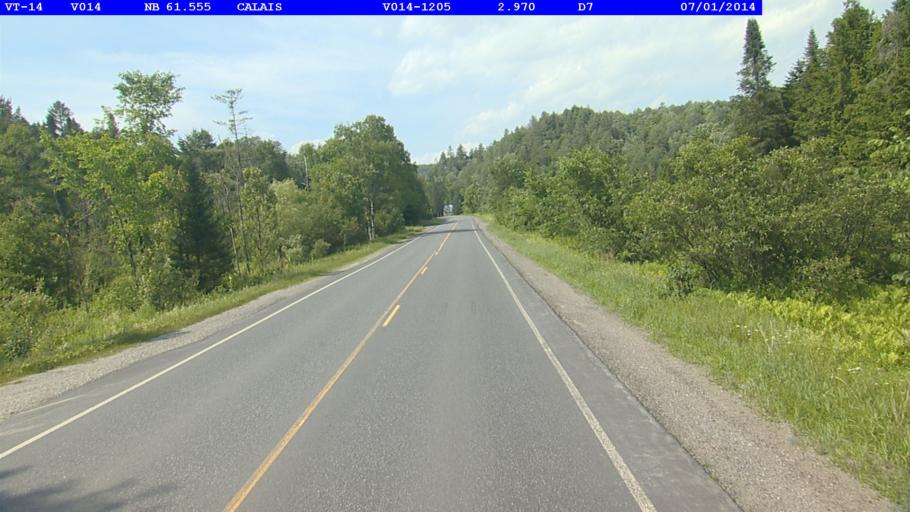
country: US
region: Vermont
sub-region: Washington County
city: Montpelier
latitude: 44.3490
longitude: -72.4419
